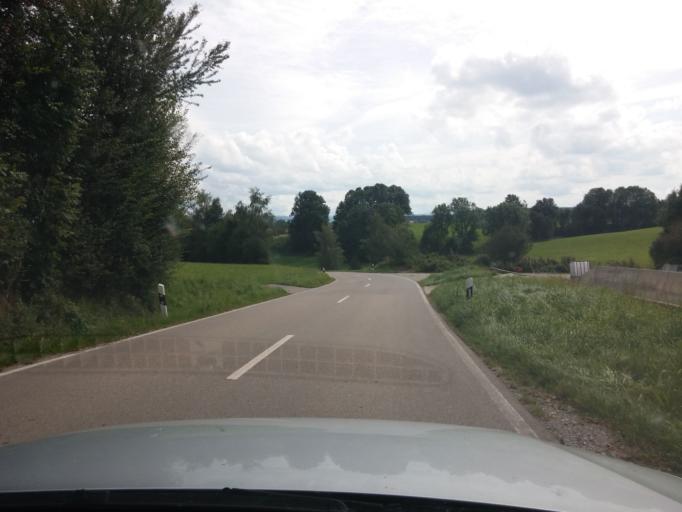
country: DE
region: Bavaria
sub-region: Swabia
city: Legau
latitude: 47.8451
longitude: 10.0880
